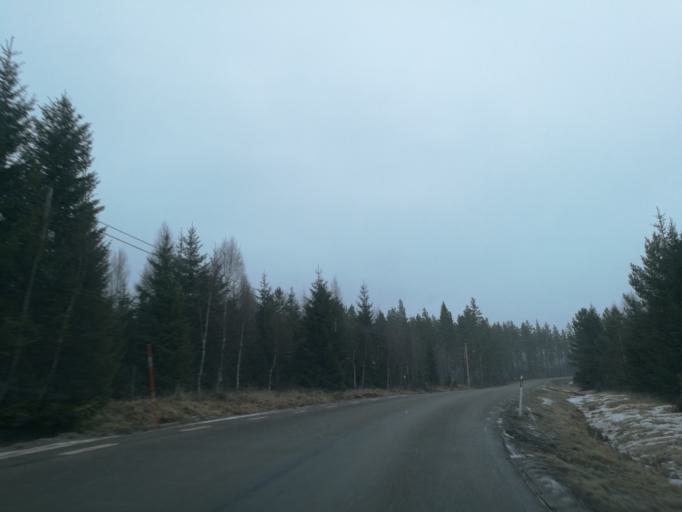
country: NO
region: Hedmark
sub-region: Asnes
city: Flisa
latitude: 60.6995
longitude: 12.5189
